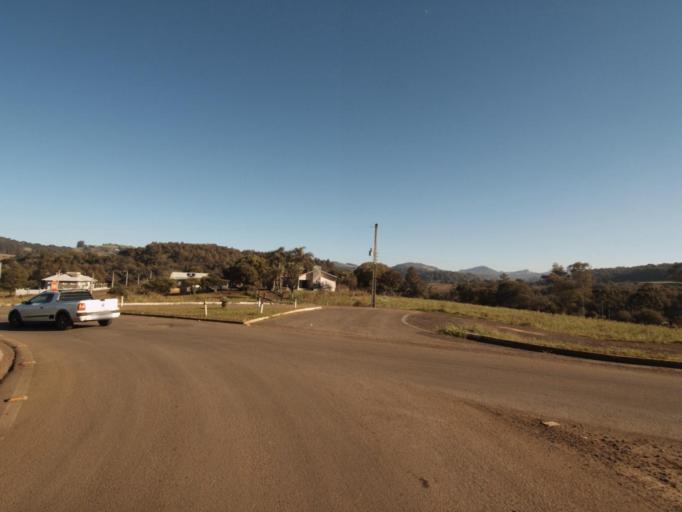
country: BR
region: Rio Grande do Sul
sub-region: Frederico Westphalen
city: Frederico Westphalen
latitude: -26.8879
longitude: -53.1772
